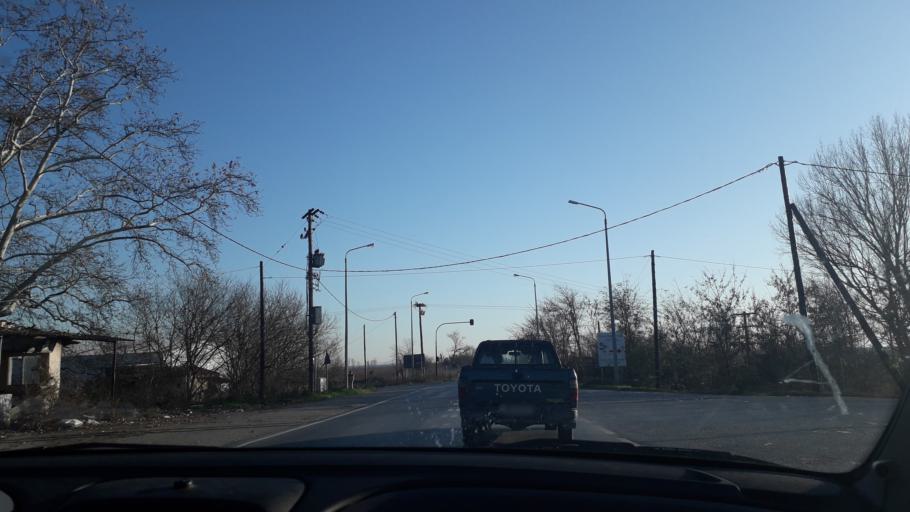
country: GR
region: Central Macedonia
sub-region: Nomos Pellis
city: Giannitsa
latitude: 40.7273
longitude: 22.4075
